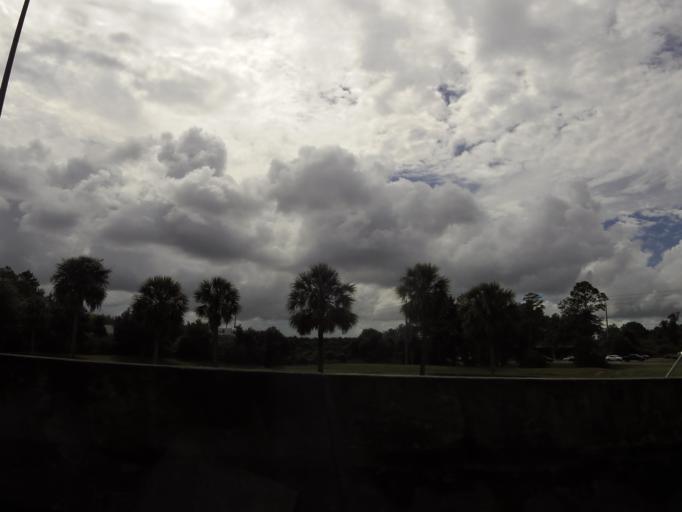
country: US
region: Florida
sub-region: Clay County
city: Orange Park
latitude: 30.1933
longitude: -81.7046
